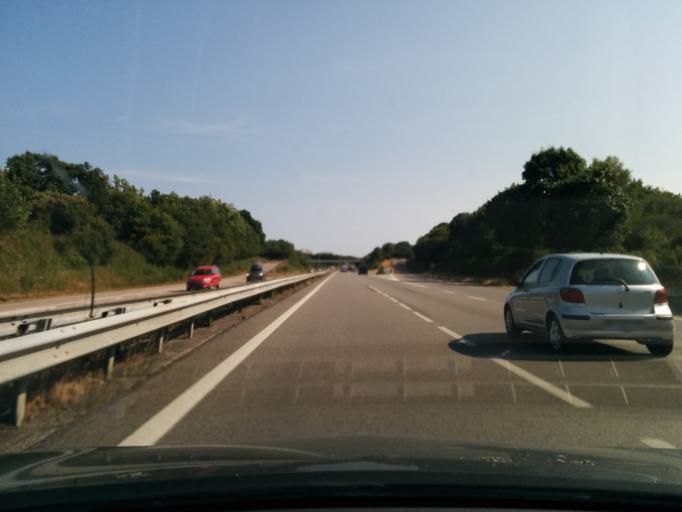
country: FR
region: Limousin
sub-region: Departement de la Haute-Vienne
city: Rilhac-Rancon
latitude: 45.8973
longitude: 1.2923
